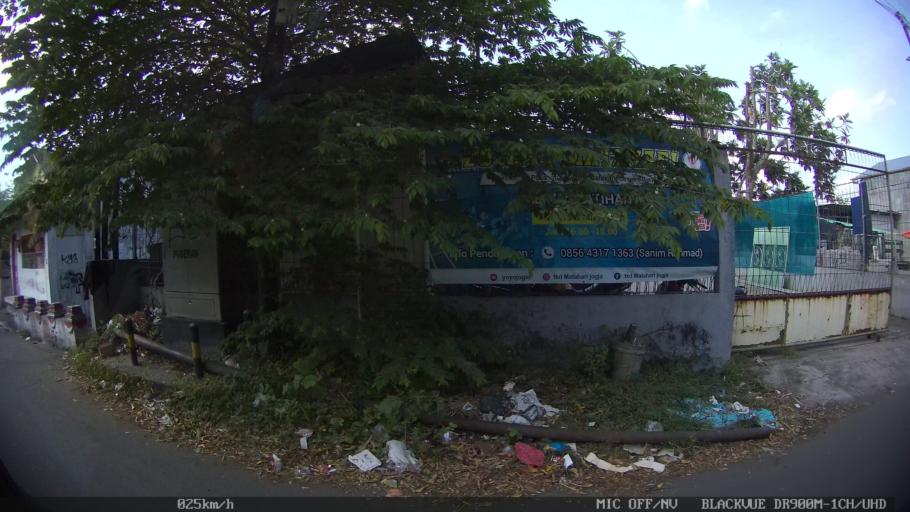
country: ID
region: Daerah Istimewa Yogyakarta
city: Kasihan
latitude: -7.8312
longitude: 110.3690
